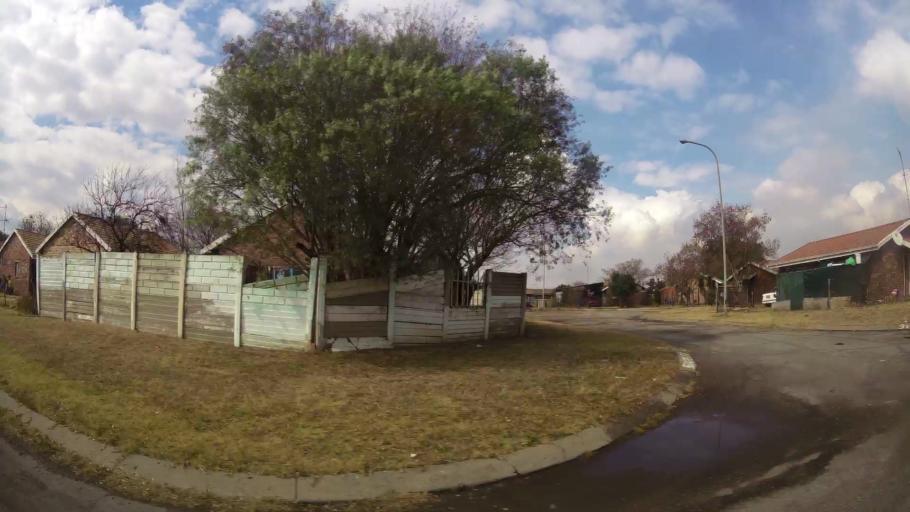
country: ZA
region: Gauteng
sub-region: Sedibeng District Municipality
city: Vereeniging
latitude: -26.6644
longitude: 27.9128
